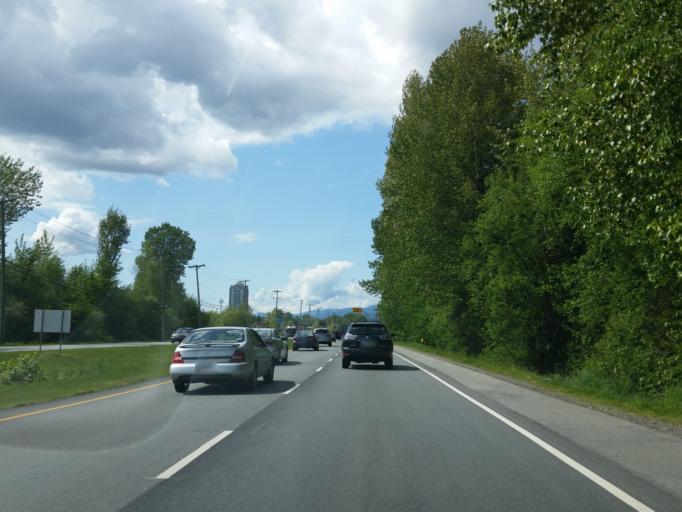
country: CA
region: British Columbia
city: Coquitlam
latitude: 49.2623
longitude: -122.7635
